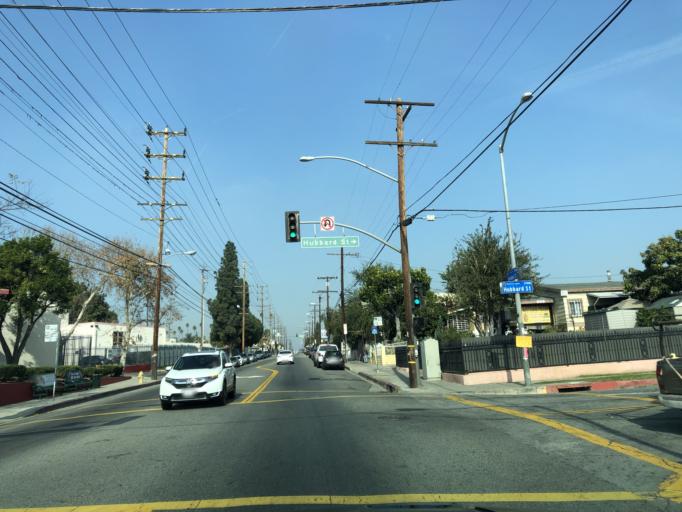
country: US
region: California
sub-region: Los Angeles County
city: Boyle Heights
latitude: 34.0260
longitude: -118.1923
